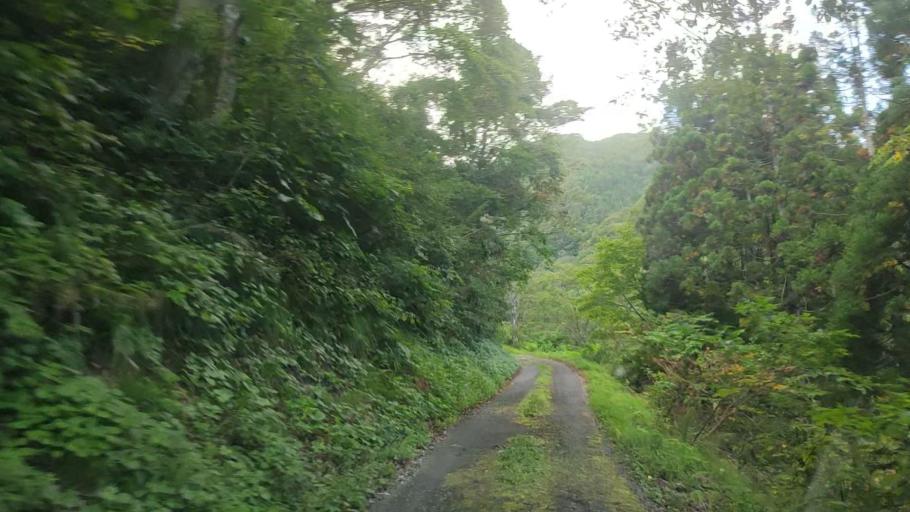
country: JP
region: Toyama
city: Yatsuomachi-higashikumisaka
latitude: 36.3272
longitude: 137.0791
